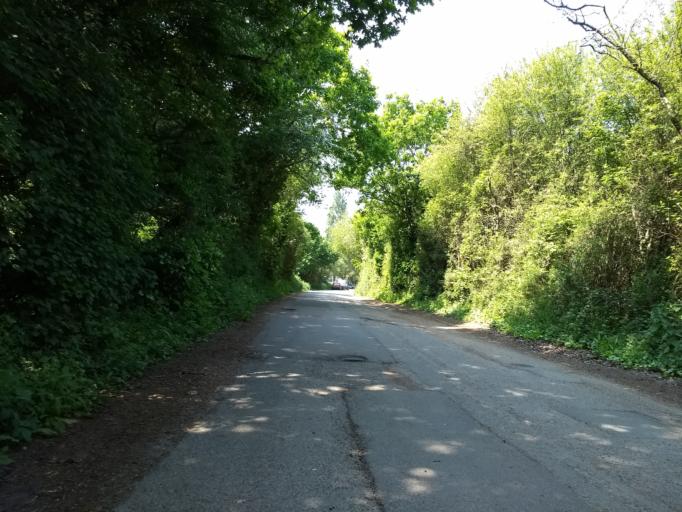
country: GB
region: England
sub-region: Isle of Wight
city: East Cowes
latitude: 50.7338
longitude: -1.2787
